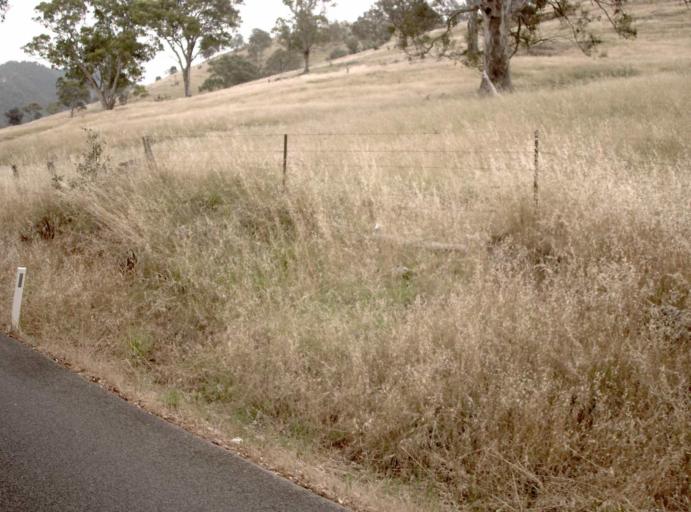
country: AU
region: Victoria
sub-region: Wellington
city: Heyfield
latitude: -37.6823
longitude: 146.6564
